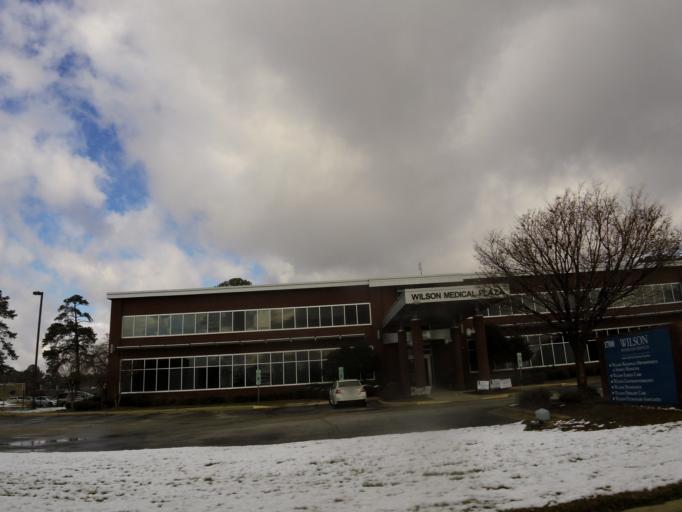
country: US
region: North Carolina
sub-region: Wilson County
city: Wilson
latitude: 35.7208
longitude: -77.9430
